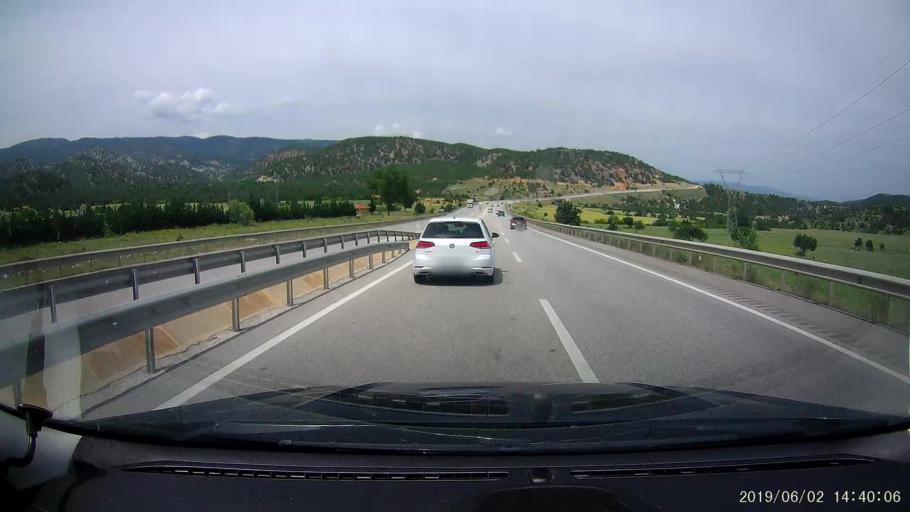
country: TR
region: Corum
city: Hacihamza
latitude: 41.0780
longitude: 34.3130
